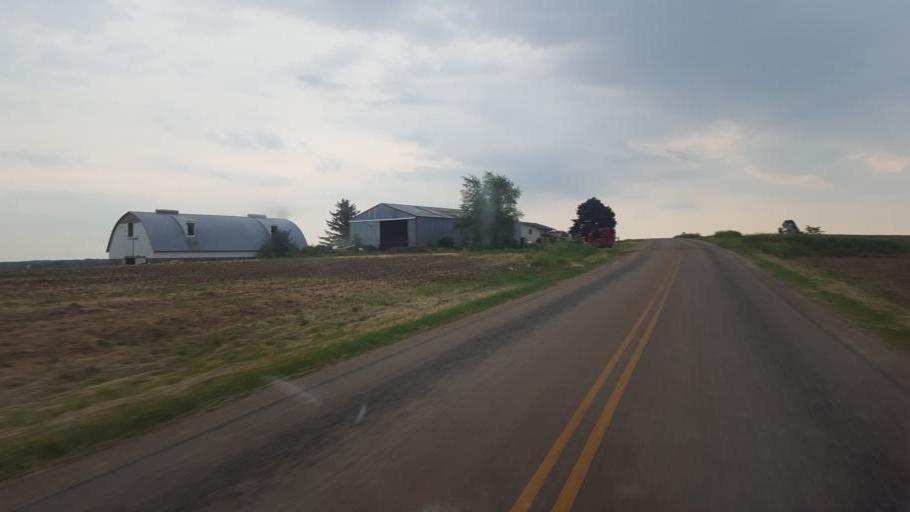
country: US
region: Wisconsin
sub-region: Vernon County
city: Hillsboro
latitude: 43.6101
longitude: -90.4381
